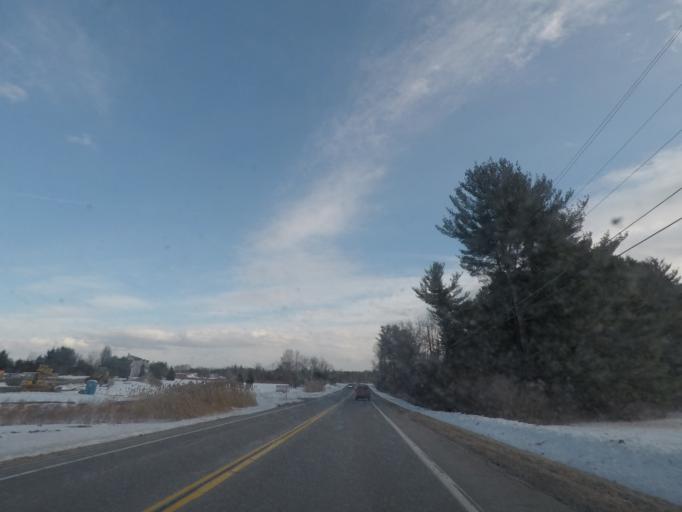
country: US
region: New York
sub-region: Schenectady County
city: Niskayuna
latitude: 42.8369
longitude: -73.8542
